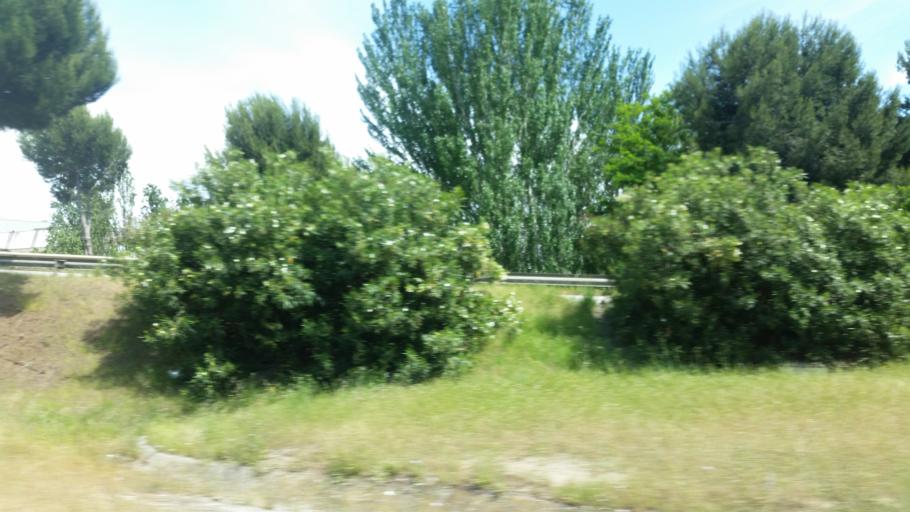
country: ES
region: Catalonia
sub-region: Provincia de Barcelona
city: El Prat de Llobregat
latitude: 41.3217
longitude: 2.0749
